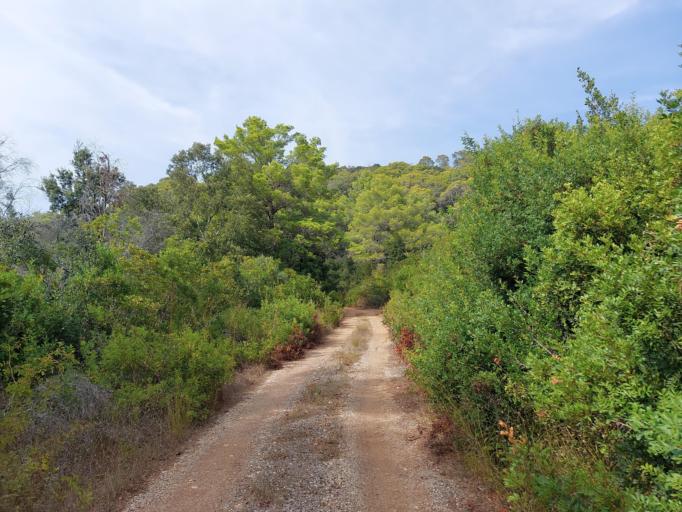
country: HR
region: Dubrovacko-Neretvanska
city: Smokvica
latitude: 42.7492
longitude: 16.8376
